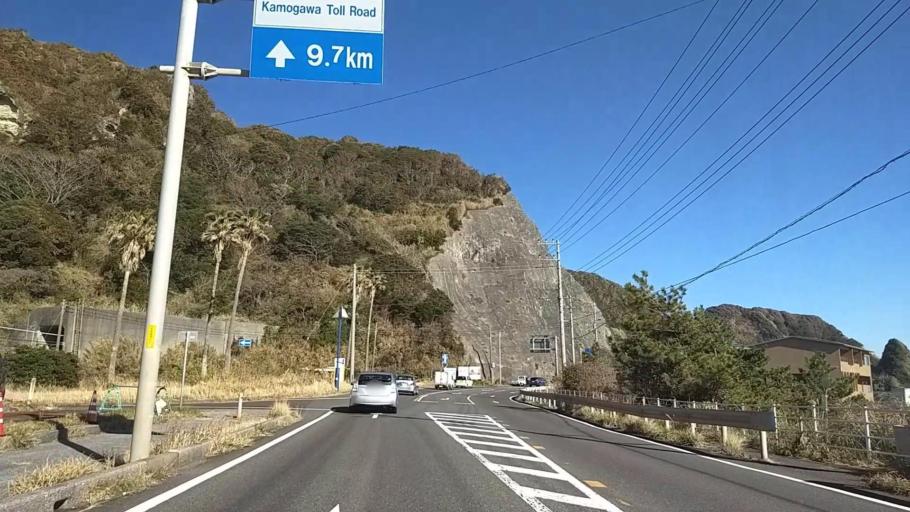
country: JP
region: Chiba
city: Kawaguchi
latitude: 35.0757
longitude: 140.0939
